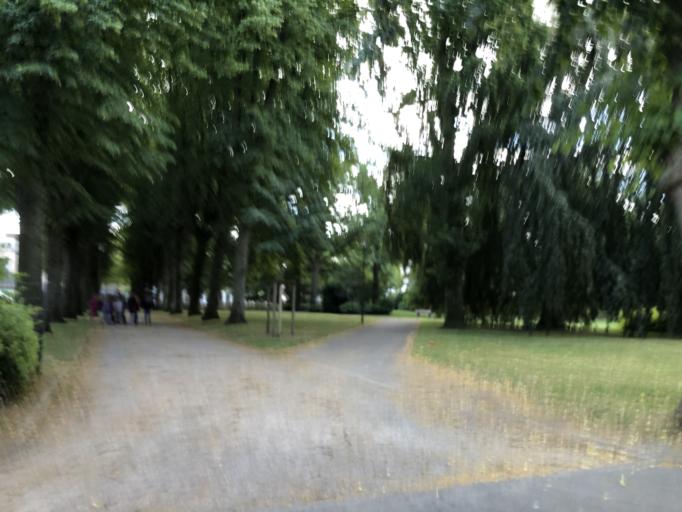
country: DE
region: North Rhine-Westphalia
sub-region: Regierungsbezirk Detmold
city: Detmold
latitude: 51.9378
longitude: 8.8724
